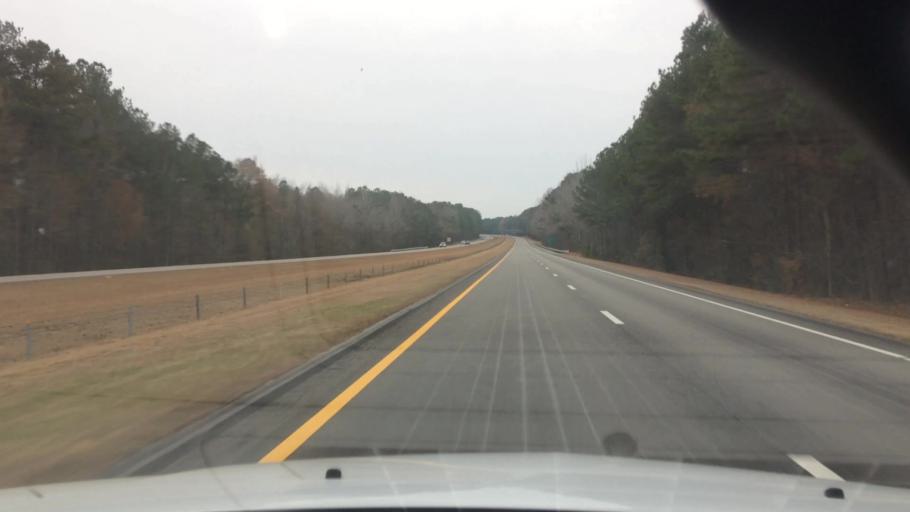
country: US
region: North Carolina
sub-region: Nash County
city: Spring Hope
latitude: 35.8893
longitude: -78.2015
